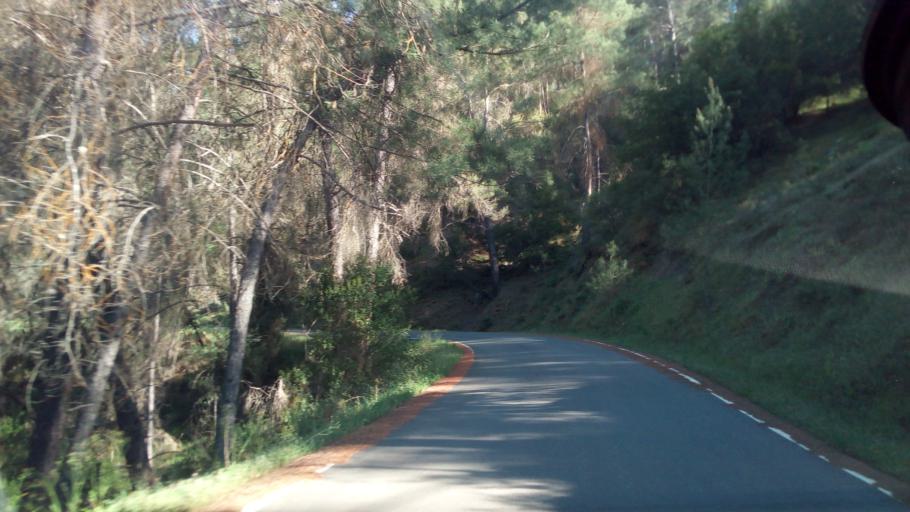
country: CY
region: Limassol
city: Pachna
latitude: 34.8886
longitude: 32.7528
